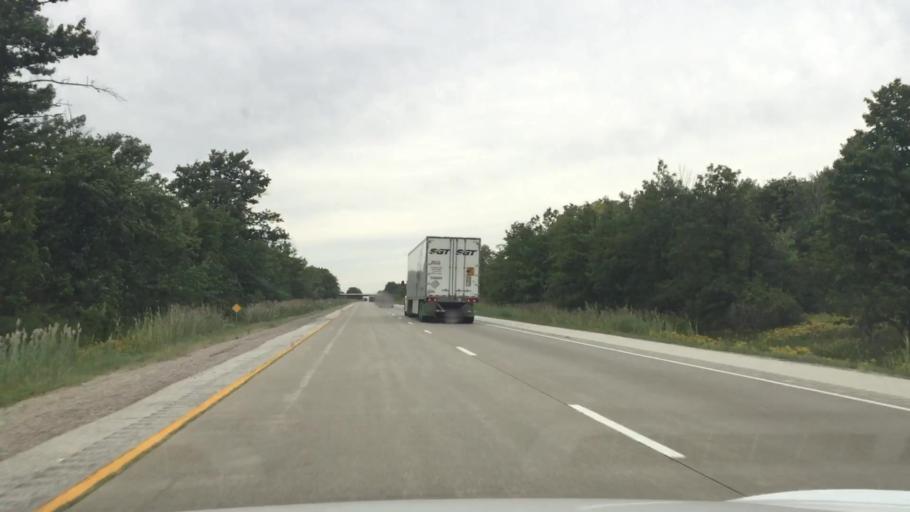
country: CA
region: Ontario
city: Camlachie
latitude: 42.9921
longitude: -82.1518
